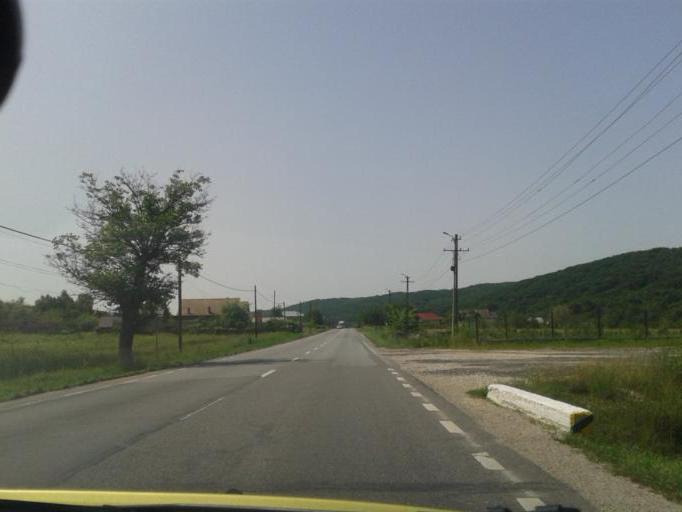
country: RO
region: Arges
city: Draganu-Olteni
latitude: 44.9191
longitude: 24.7211
